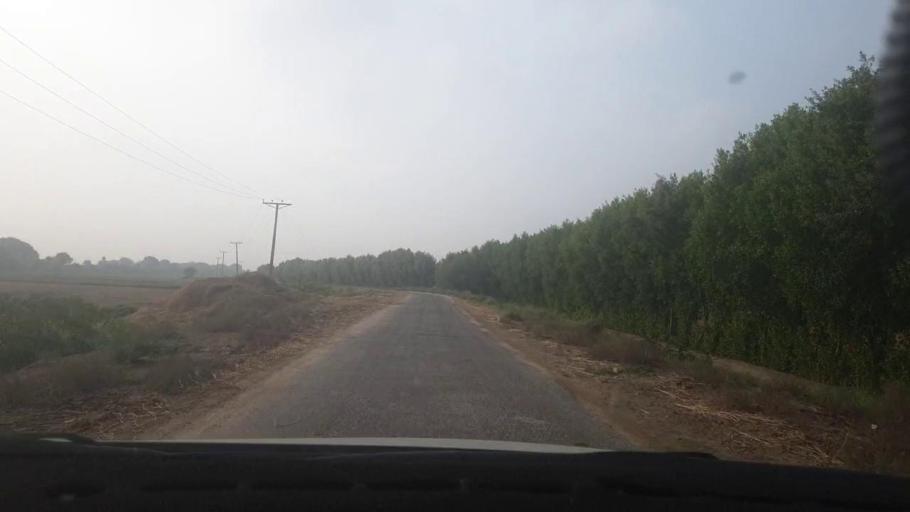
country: PK
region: Sindh
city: Tando Muhammad Khan
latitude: 25.0995
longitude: 68.5161
